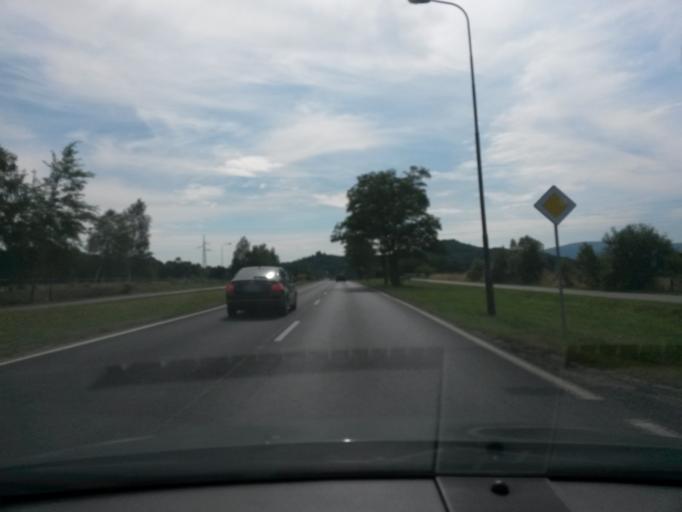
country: PL
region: Lower Silesian Voivodeship
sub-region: Powiat jeleniogorski
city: Jezow Sudecki
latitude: 50.9119
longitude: 15.7823
